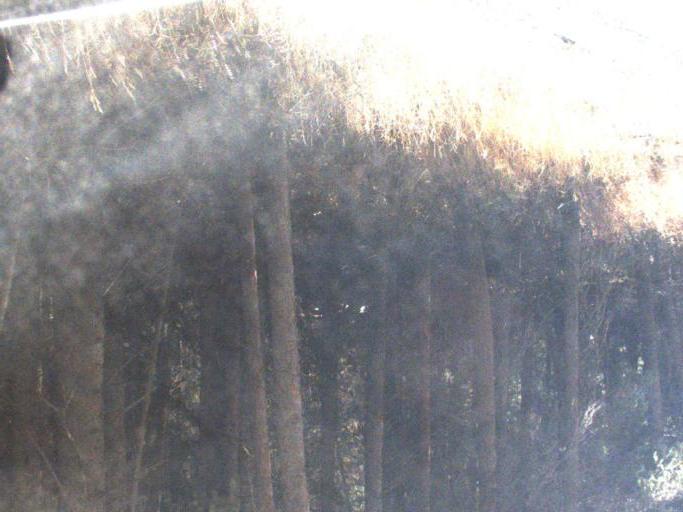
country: US
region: Washington
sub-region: Ferry County
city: Republic
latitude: 48.6303
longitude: -118.6766
